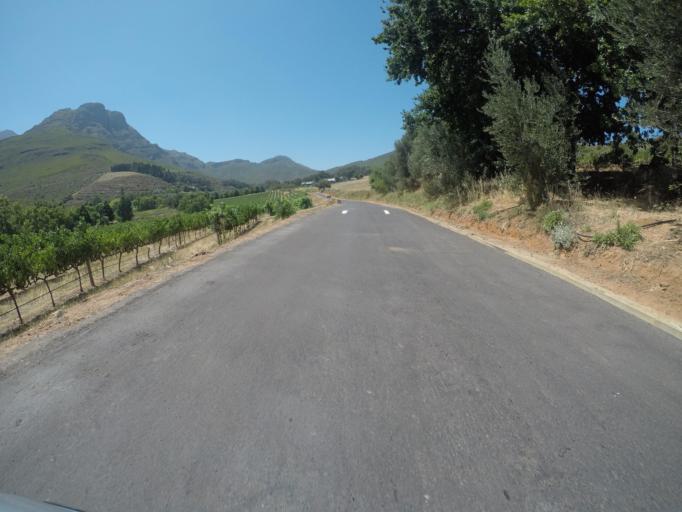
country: ZA
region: Western Cape
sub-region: Cape Winelands District Municipality
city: Stellenbosch
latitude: -33.9987
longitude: 18.8823
